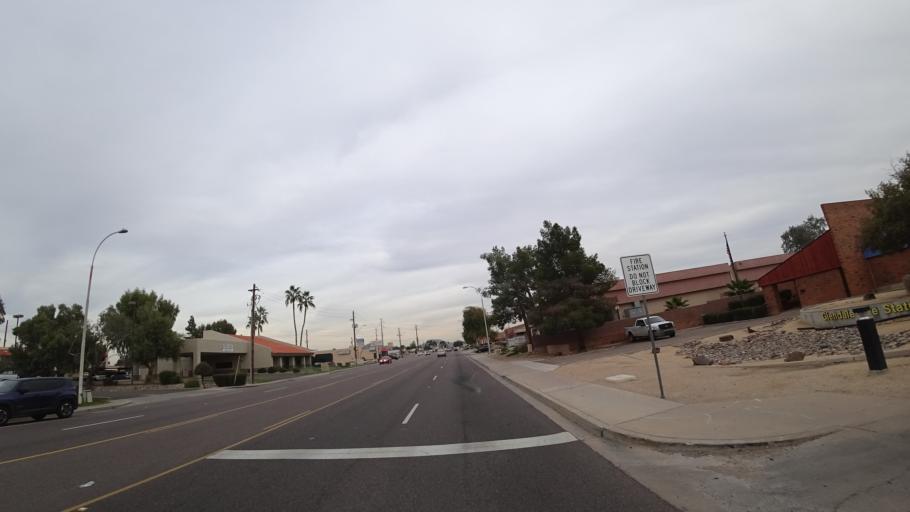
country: US
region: Arizona
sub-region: Maricopa County
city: Glendale
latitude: 33.5819
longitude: -112.1548
